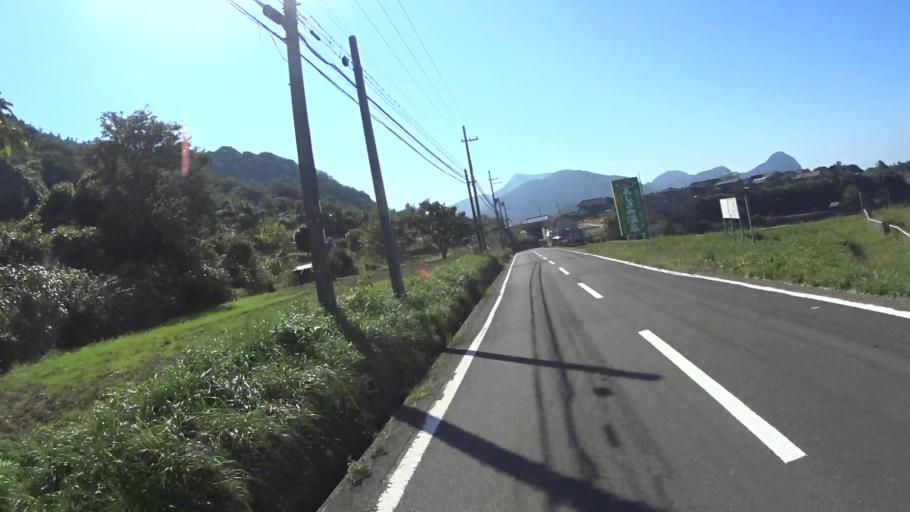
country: JP
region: Kyoto
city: Miyazu
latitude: 35.7607
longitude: 135.1833
